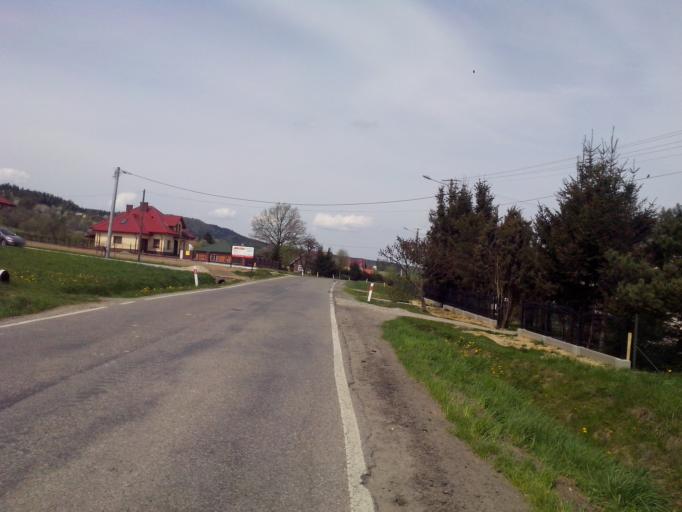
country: PL
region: Subcarpathian Voivodeship
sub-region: Powiat strzyzowski
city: Jawornik
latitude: 49.8082
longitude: 21.8526
